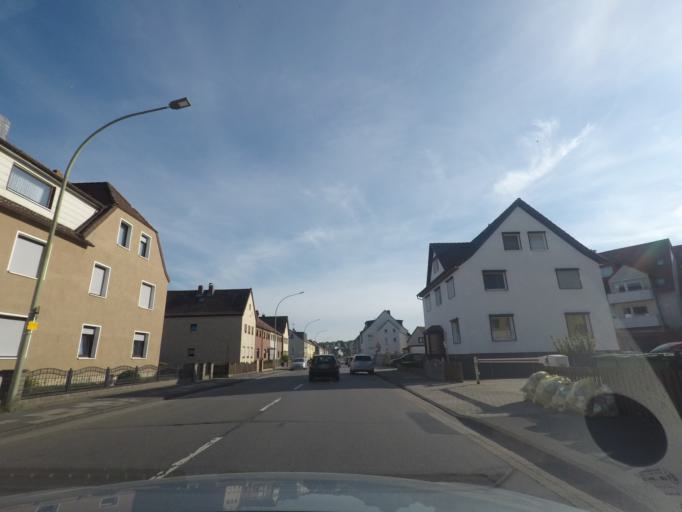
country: DE
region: Lower Saxony
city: Helmstedt
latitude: 52.2342
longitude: 10.9995
